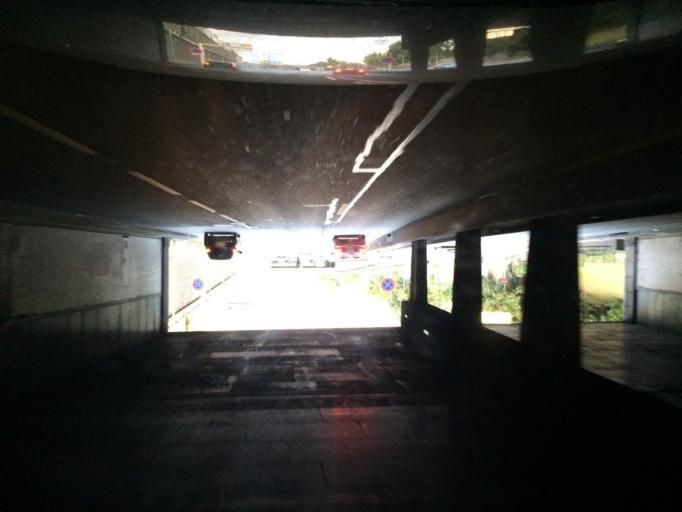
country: FR
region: Ile-de-France
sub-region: Departement des Hauts-de-Seine
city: Montrouge
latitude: 48.8210
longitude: 2.3208
